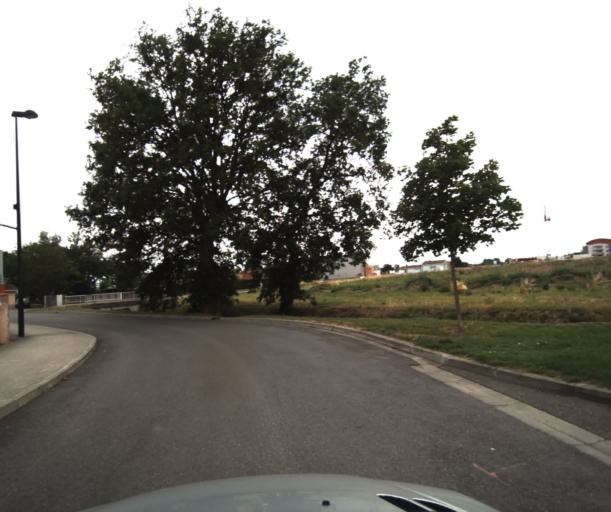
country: FR
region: Midi-Pyrenees
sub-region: Departement de la Haute-Garonne
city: Labarthe-sur-Leze
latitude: 43.4539
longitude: 1.3977
